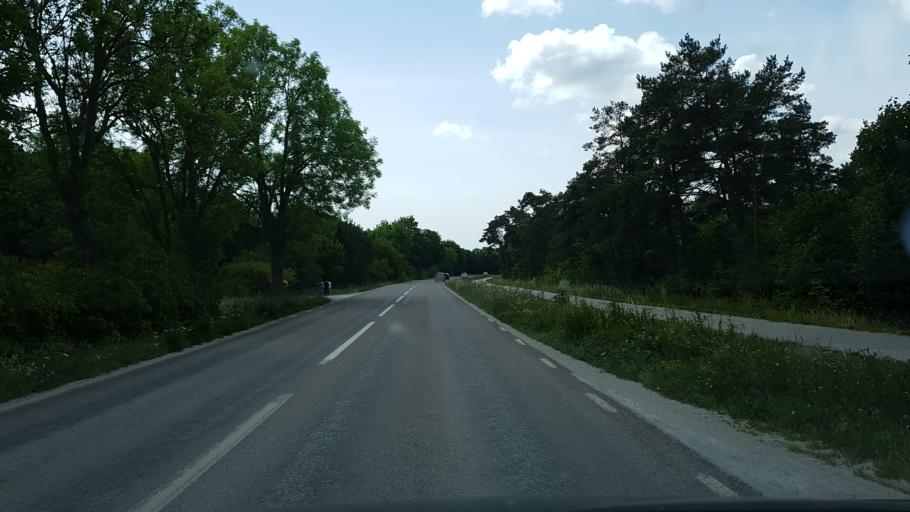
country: SE
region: Gotland
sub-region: Gotland
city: Visby
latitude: 57.7497
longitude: 18.4214
